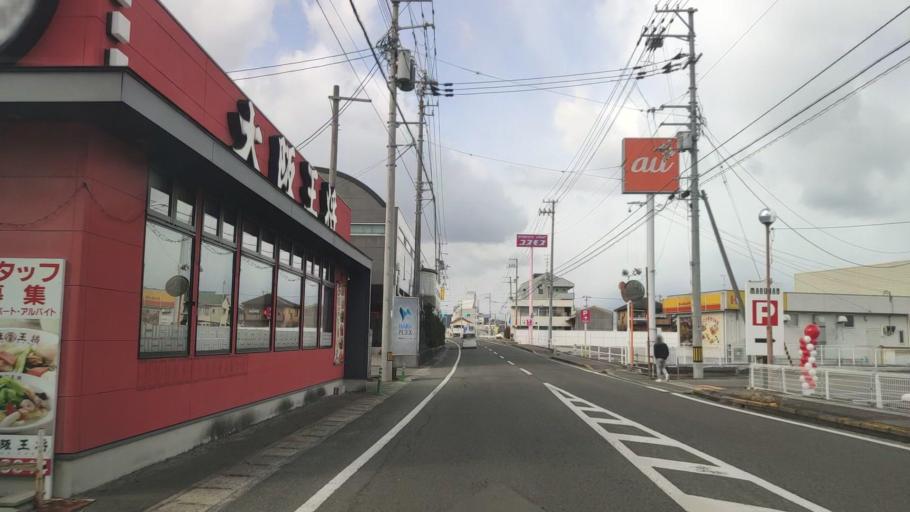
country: JP
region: Ehime
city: Saijo
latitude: 34.0470
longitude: 133.0190
